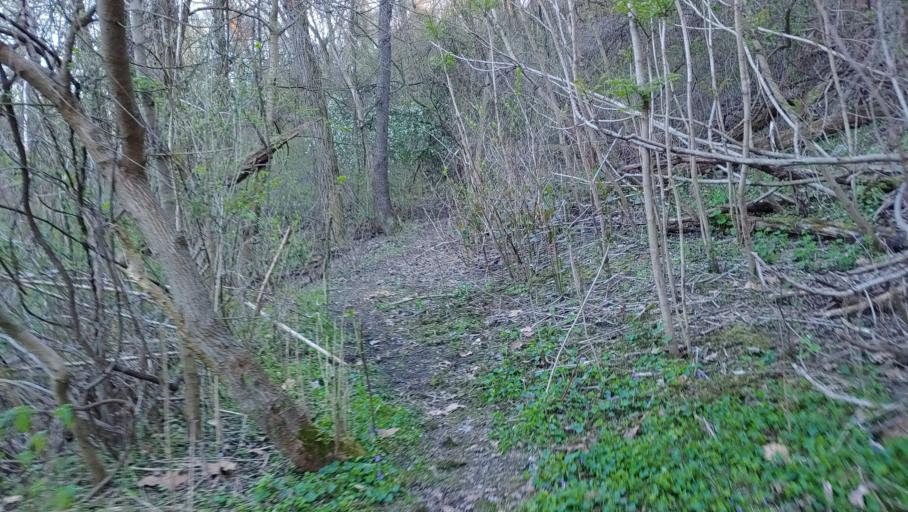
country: US
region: Pennsylvania
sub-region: Allegheny County
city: Green Tree
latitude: 40.4261
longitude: -80.0258
